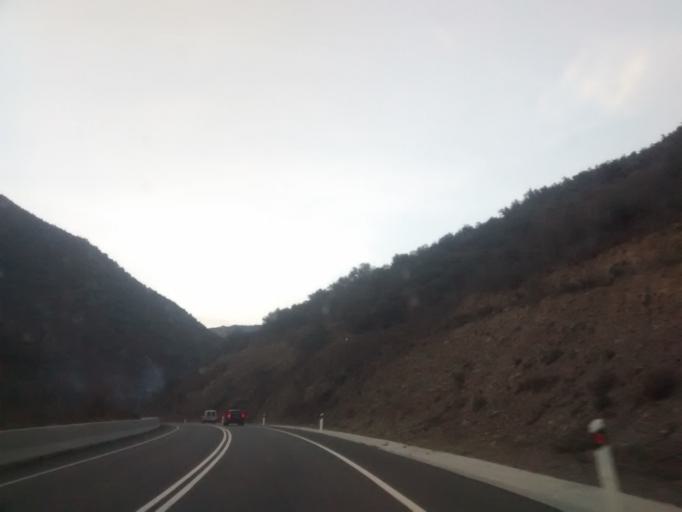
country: ES
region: Catalonia
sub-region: Provincia de Lleida
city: la Seu d'Urgell
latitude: 42.4110
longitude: 1.4683
